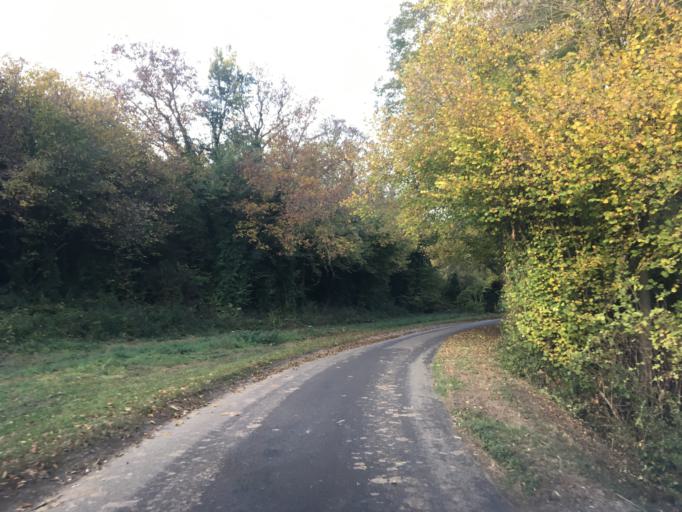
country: FR
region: Haute-Normandie
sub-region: Departement de l'Eure
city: Heudreville-sur-Eure
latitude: 49.0988
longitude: 1.2237
